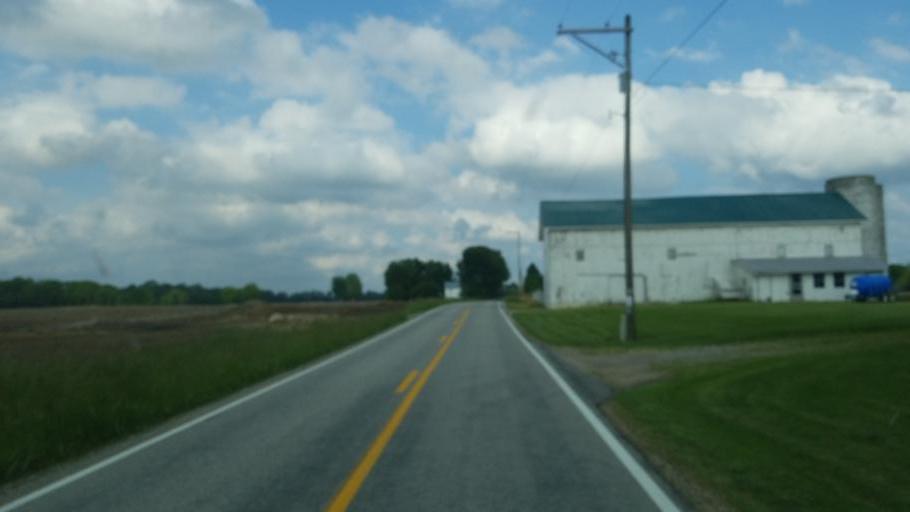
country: US
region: Ohio
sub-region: Delaware County
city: Sunbury
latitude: 40.2175
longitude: -82.8453
